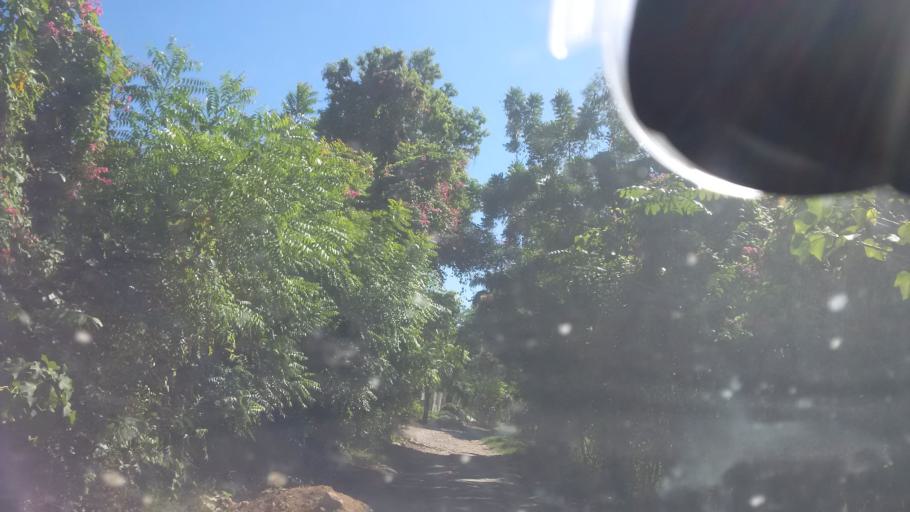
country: HT
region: Ouest
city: Grangwav
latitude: 18.4292
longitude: -72.7870
